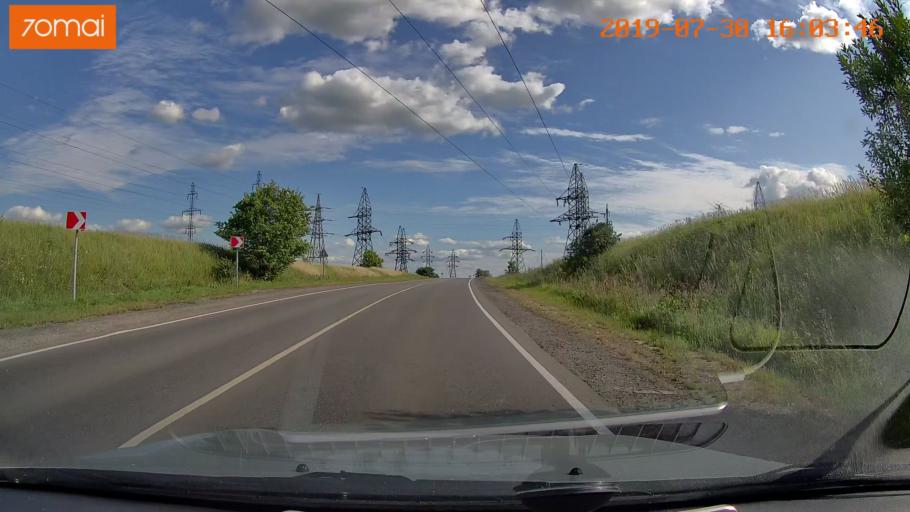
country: RU
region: Moskovskaya
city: Voskresensk
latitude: 55.2876
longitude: 38.6995
